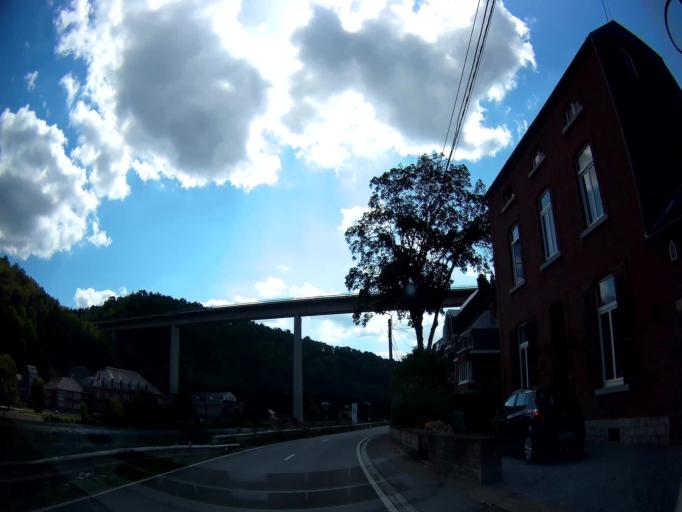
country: BE
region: Wallonia
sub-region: Province de Namur
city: Dinant
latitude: 50.2443
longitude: 4.9196
